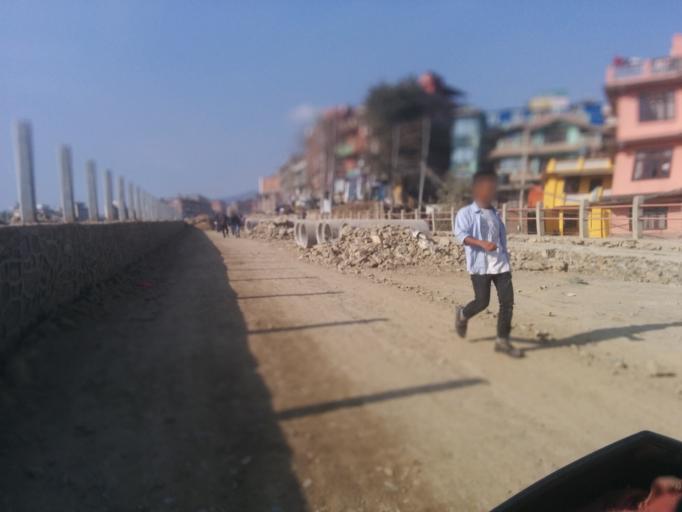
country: NP
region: Central Region
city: Kirtipur
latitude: 27.6911
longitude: 85.2830
